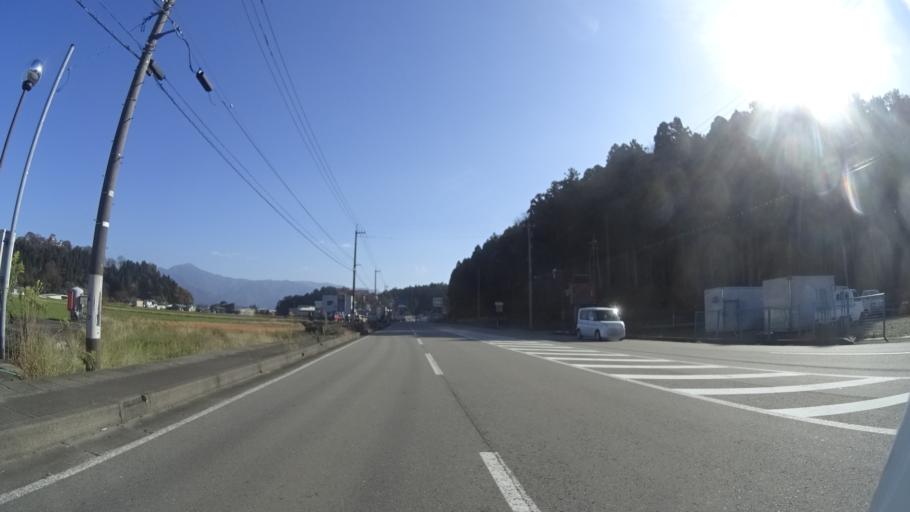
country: JP
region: Fukui
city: Ono
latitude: 35.9876
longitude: 136.4749
